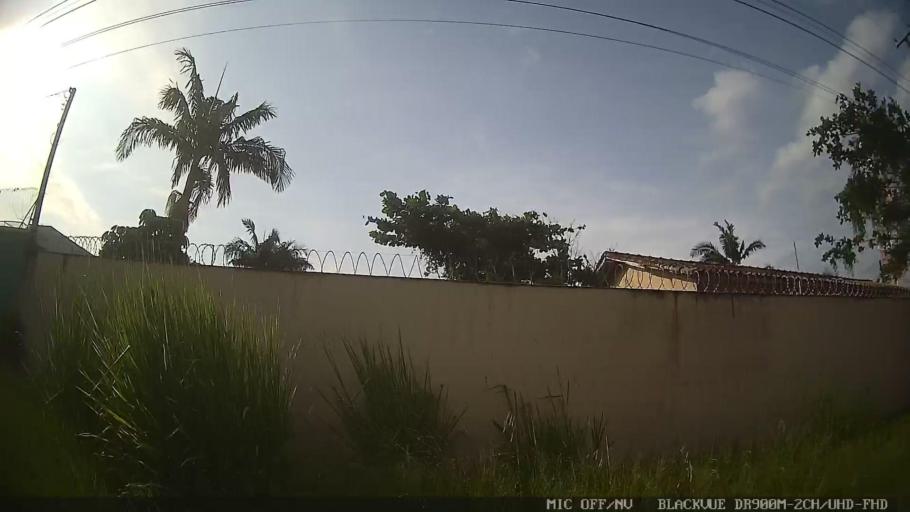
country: BR
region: Sao Paulo
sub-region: Bertioga
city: Bertioga
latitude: -23.8171
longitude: -46.0437
